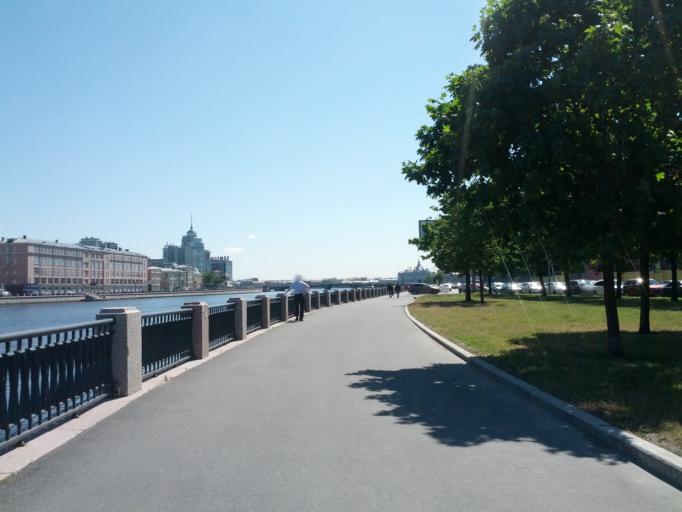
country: RU
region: Leningrad
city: Sampsonievskiy
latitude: 59.9653
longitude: 30.3346
